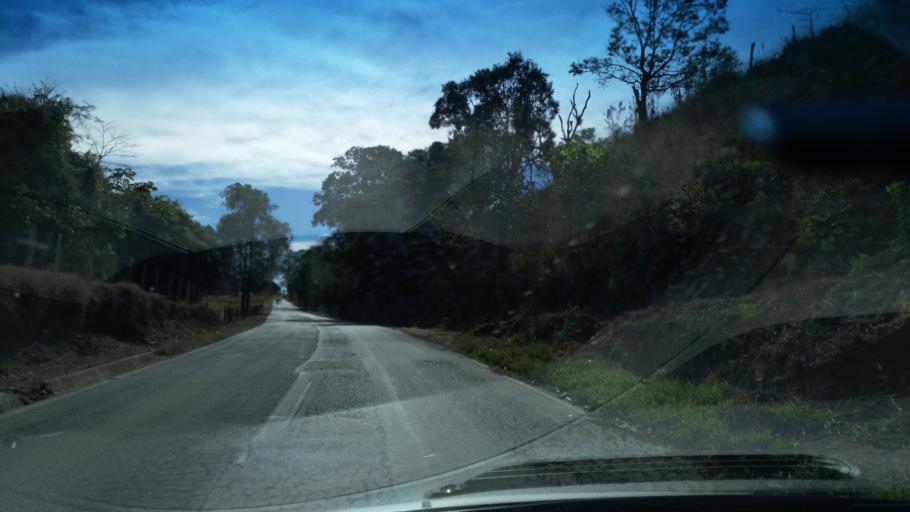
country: BR
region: Minas Gerais
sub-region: Andradas
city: Andradas
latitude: -22.0513
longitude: -46.3602
